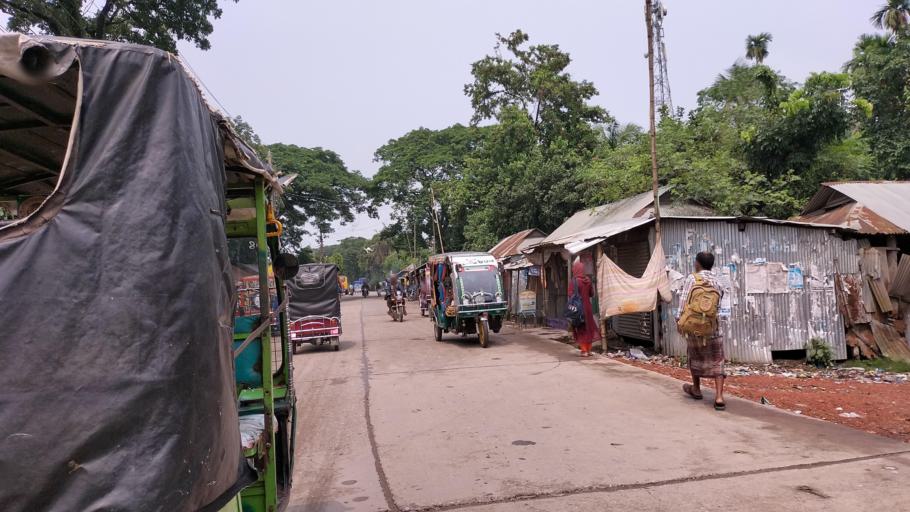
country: BD
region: Dhaka
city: Netrakona
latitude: 24.8940
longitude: 90.7399
